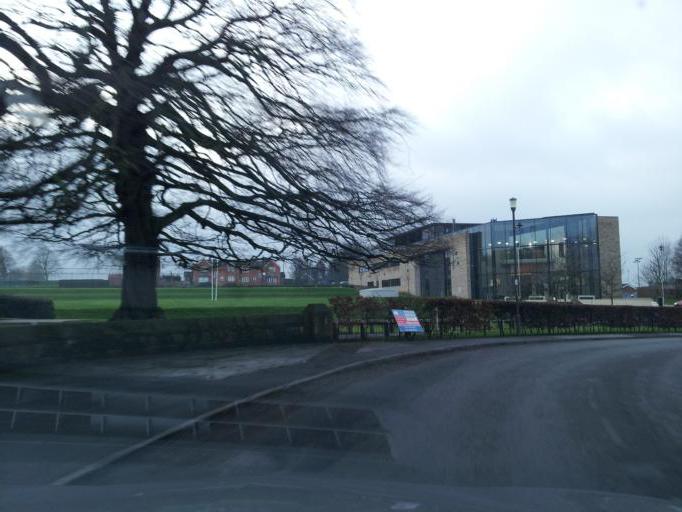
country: GB
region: England
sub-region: Derbyshire
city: Repton
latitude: 52.8405
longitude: -1.5531
